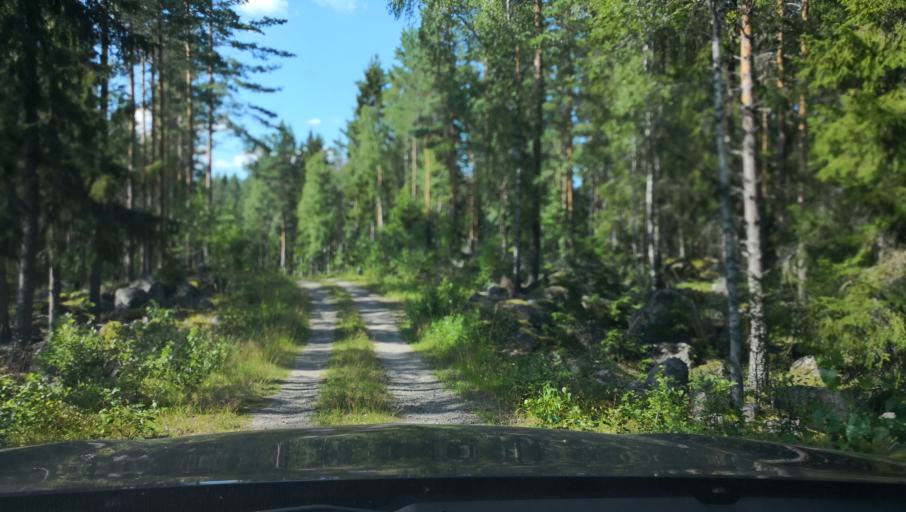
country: SE
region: Vaestmanland
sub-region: Vasteras
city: Skultuna
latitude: 59.7148
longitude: 16.3621
